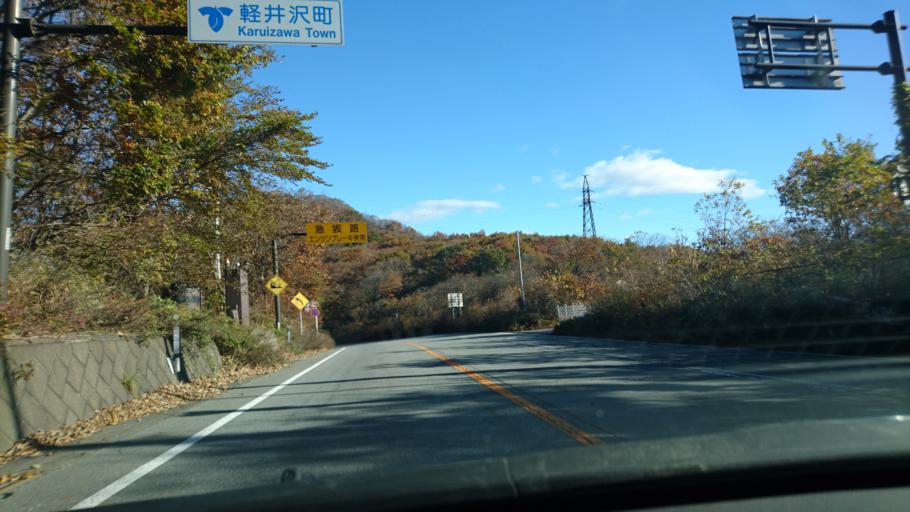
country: JP
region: Nagano
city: Saku
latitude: 36.3194
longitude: 138.6502
